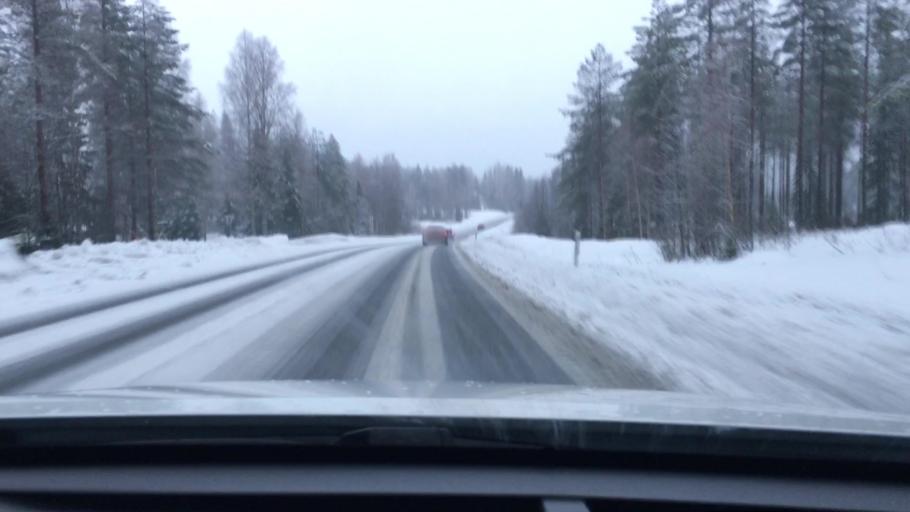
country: FI
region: Northern Savo
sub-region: Ylae-Savo
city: Sonkajaervi
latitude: 63.7647
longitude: 27.4104
